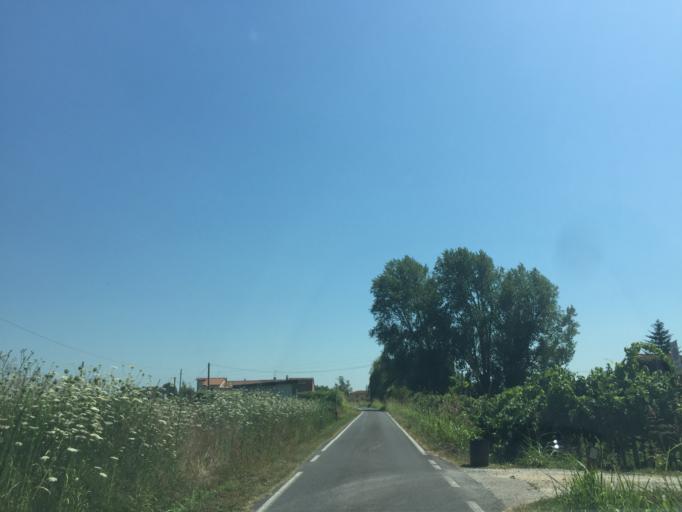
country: IT
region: Tuscany
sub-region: Provincia di Pistoia
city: Chiesina Uzzanese
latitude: 43.8367
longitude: 10.7336
